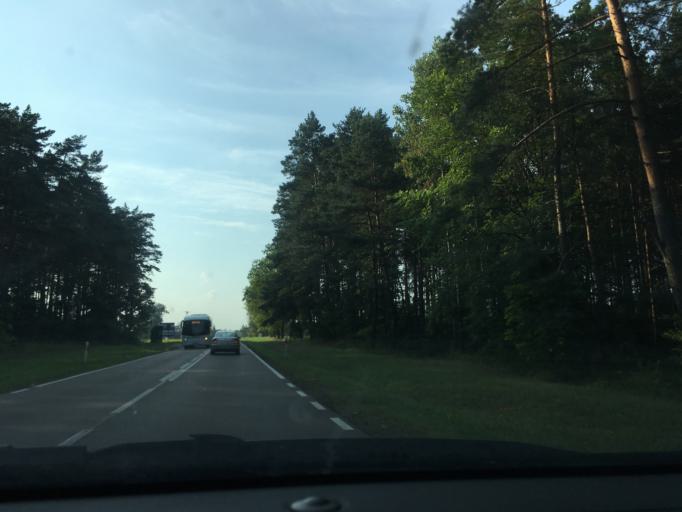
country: PL
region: Podlasie
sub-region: Powiat bialostocki
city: Dobrzyniewo Duze
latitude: 53.2552
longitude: 22.9817
